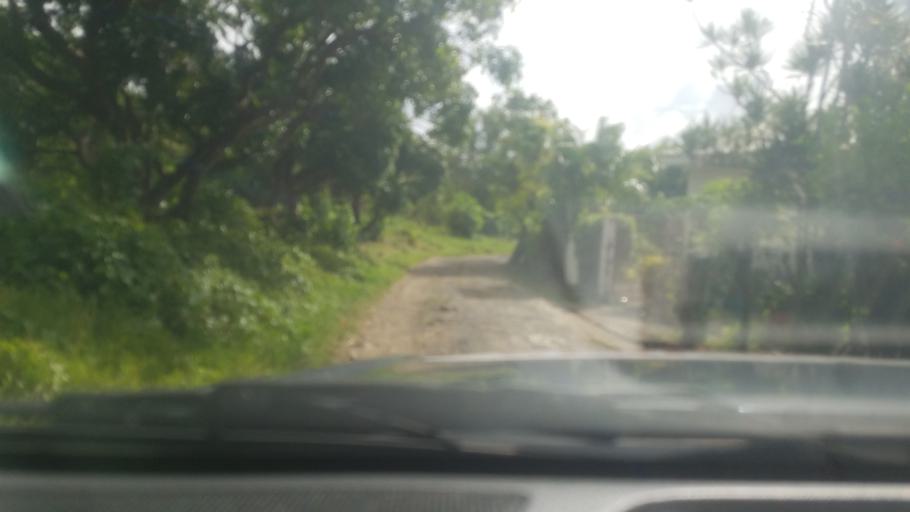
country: LC
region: Micoud Quarter
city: Micoud
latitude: 13.7955
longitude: -60.9157
